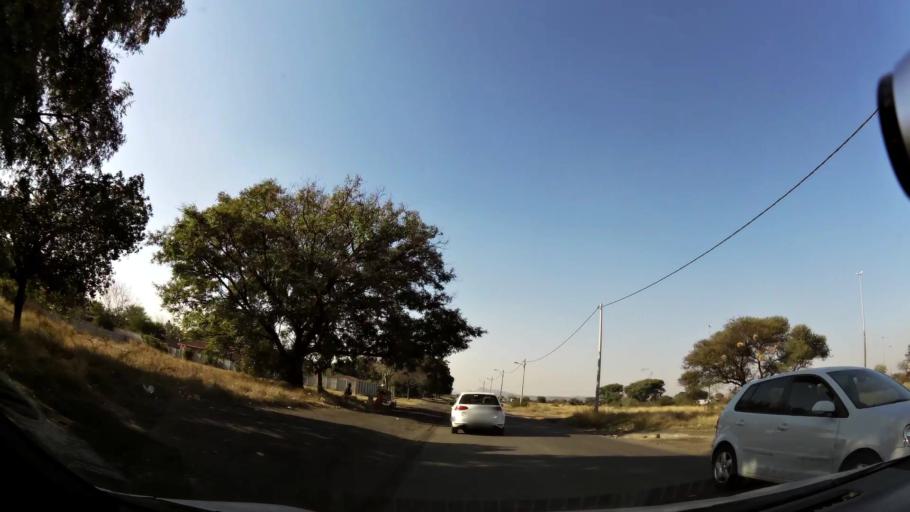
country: ZA
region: North-West
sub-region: Bojanala Platinum District Municipality
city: Rustenburg
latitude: -25.6626
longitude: 27.2629
